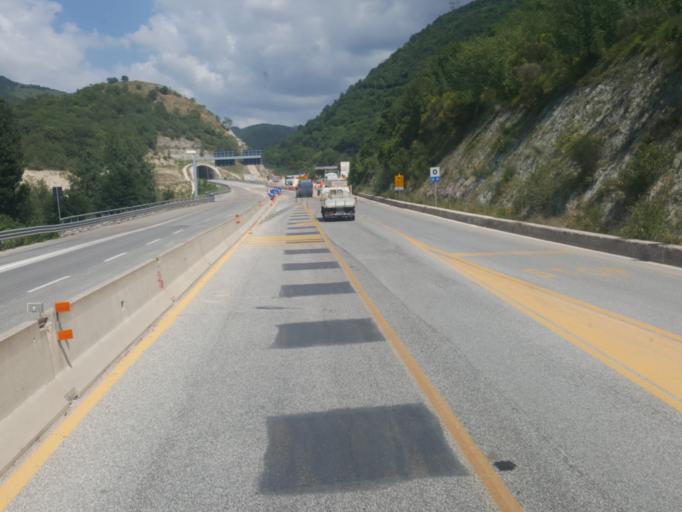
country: IT
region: Umbria
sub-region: Provincia di Perugia
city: Fossato di Vico
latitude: 43.3002
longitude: 12.7595
